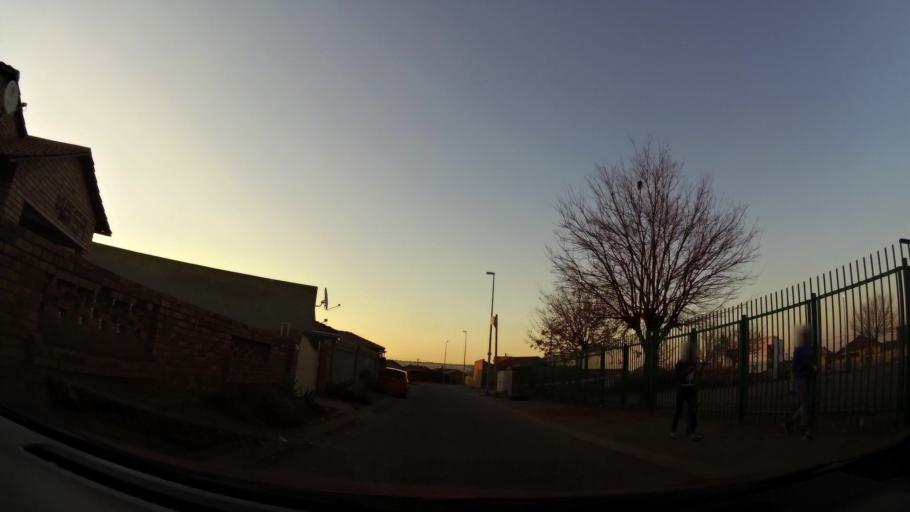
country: ZA
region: Gauteng
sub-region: City of Johannesburg Metropolitan Municipality
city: Soweto
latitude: -26.2269
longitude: 27.8426
